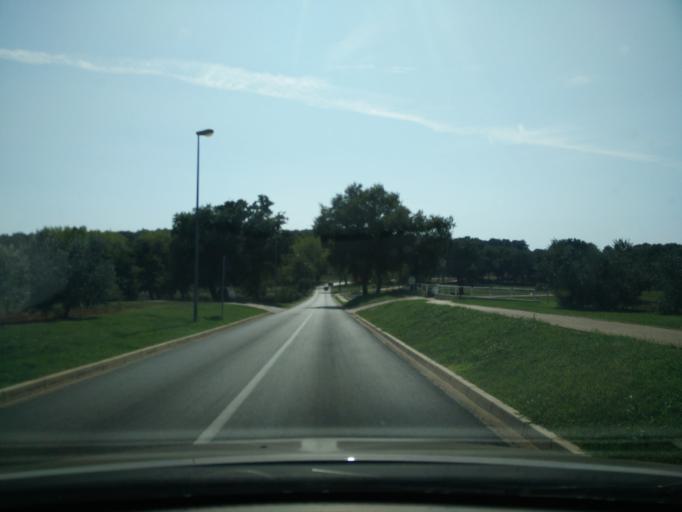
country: HR
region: Istarska
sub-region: Grad Porec
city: Porec
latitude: 45.2032
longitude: 13.6018
